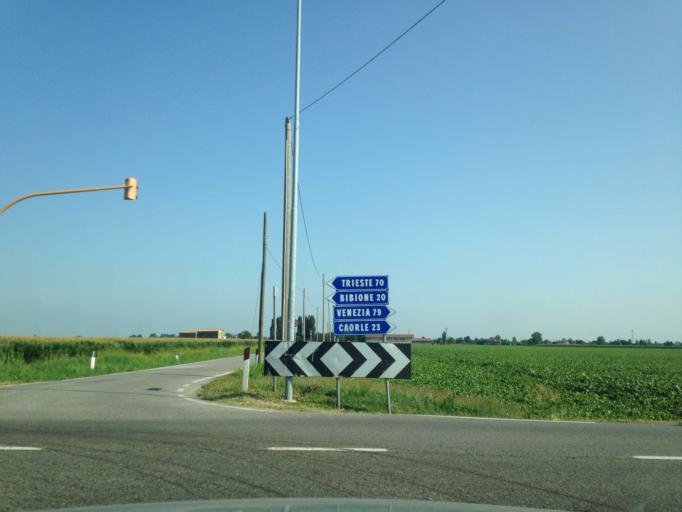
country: IT
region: Veneto
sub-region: Provincia di Venezia
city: Lugugnana
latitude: 45.7272
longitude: 12.9343
